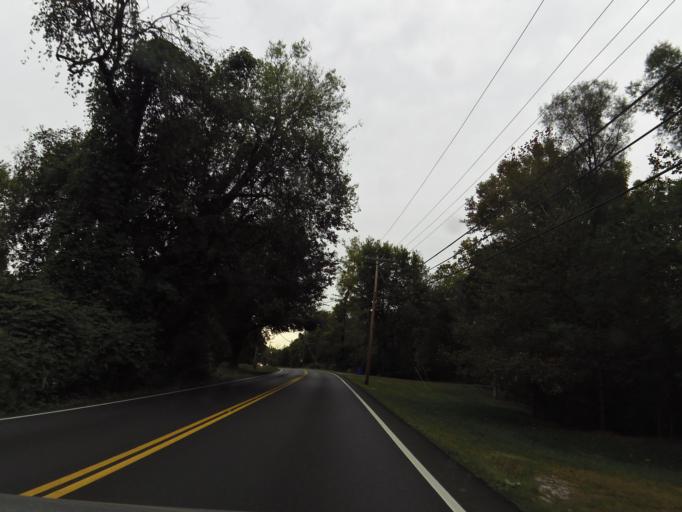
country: US
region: Tennessee
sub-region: Blount County
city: Louisville
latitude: 35.8853
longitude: -84.0384
